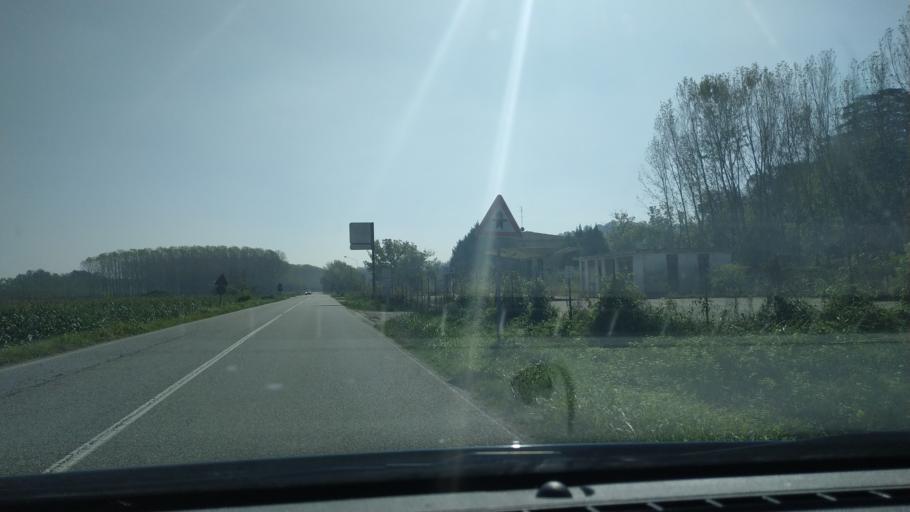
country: IT
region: Piedmont
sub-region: Provincia di Alessandria
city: Pomaro Monferrato
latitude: 45.0654
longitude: 8.5977
